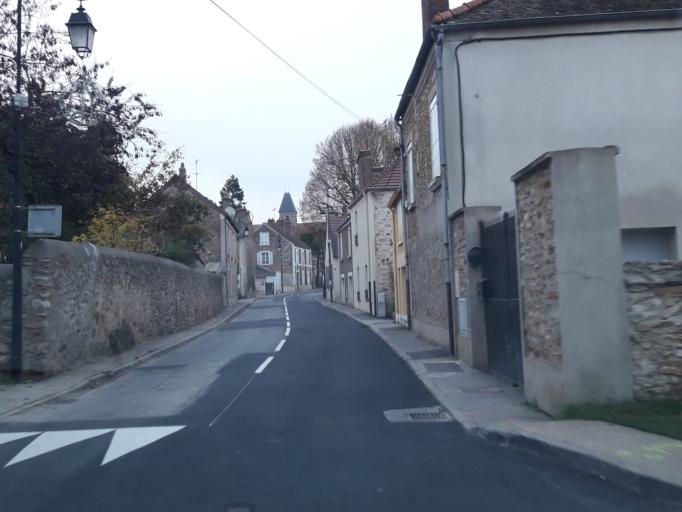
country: FR
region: Ile-de-France
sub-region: Departement de l'Essonne
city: Vert-le-Petit
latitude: 48.5498
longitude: 2.3664
